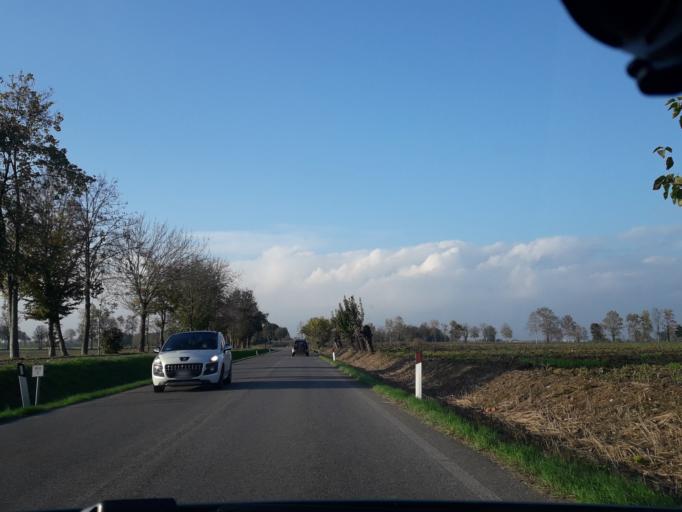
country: IT
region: Friuli Venezia Giulia
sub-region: Provincia di Udine
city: Pradamano
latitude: 46.0398
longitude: 13.2899
